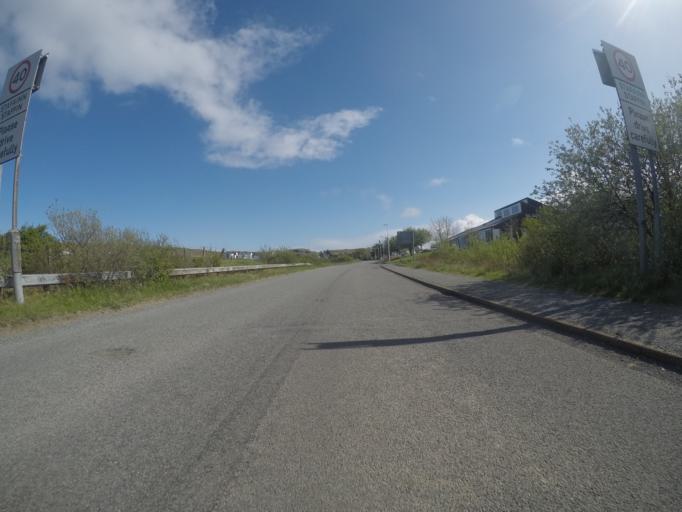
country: GB
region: Scotland
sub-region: Highland
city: Portree
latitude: 57.6291
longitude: -6.2104
